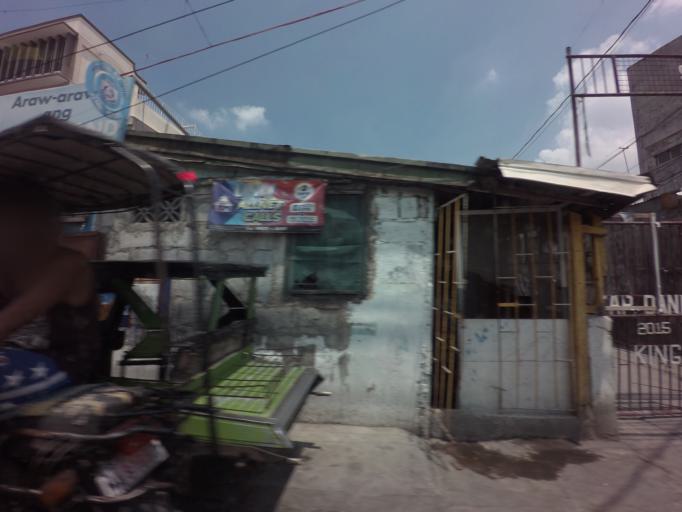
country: PH
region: Calabarzon
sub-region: Province of Laguna
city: San Pedro
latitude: 14.4035
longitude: 121.0502
